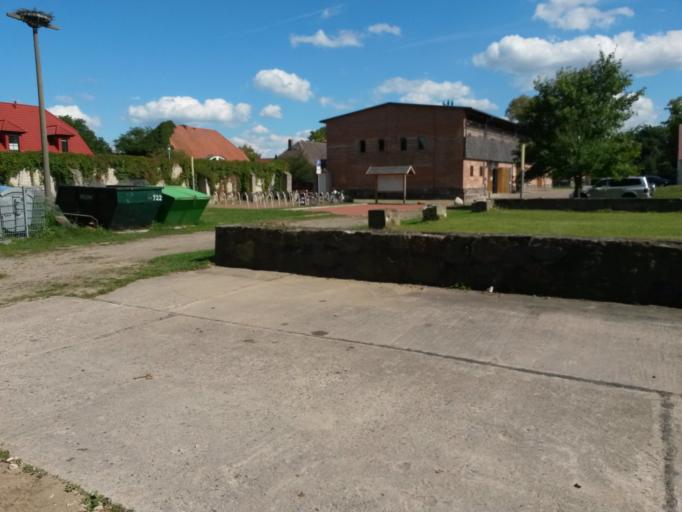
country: DE
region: Brandenburg
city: Meyenburg
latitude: 53.0123
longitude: 14.2219
